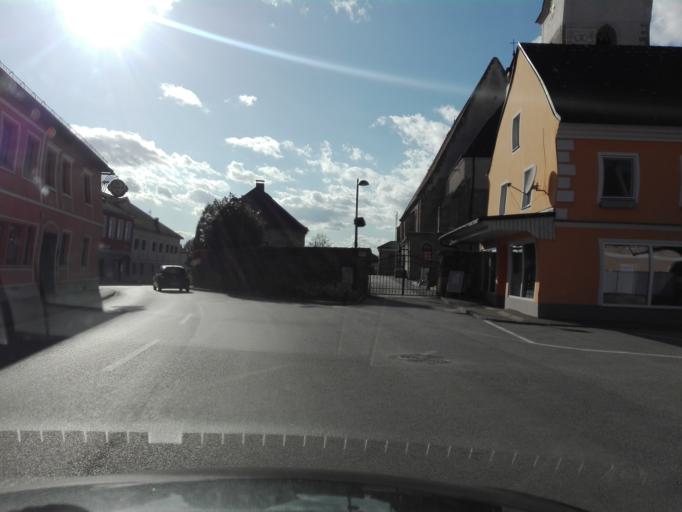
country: AT
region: Upper Austria
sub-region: Politischer Bezirk Perg
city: Perg
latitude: 48.2257
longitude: 14.6095
